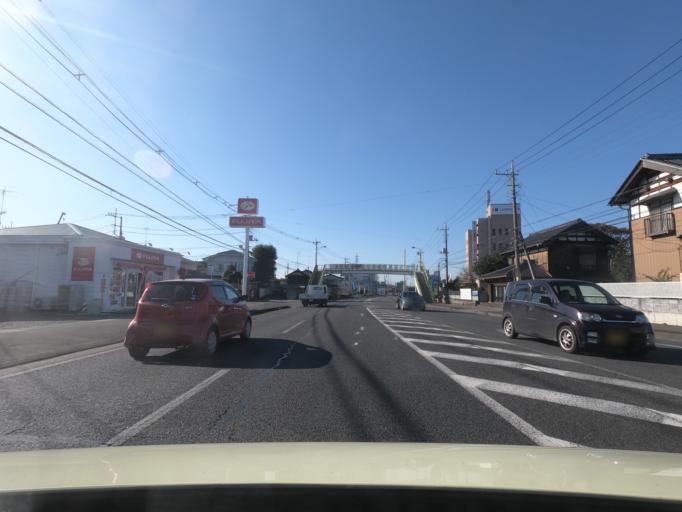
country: JP
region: Ibaraki
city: Ishige
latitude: 36.1782
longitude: 139.9567
